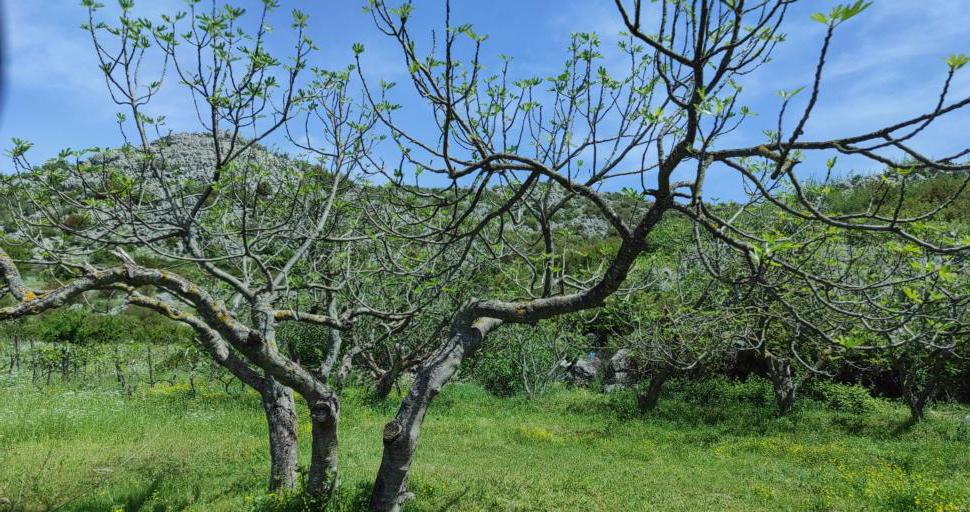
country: AL
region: Shkoder
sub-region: Rrethi i Malesia e Madhe
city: Gruemire
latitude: 42.1447
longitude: 19.5452
